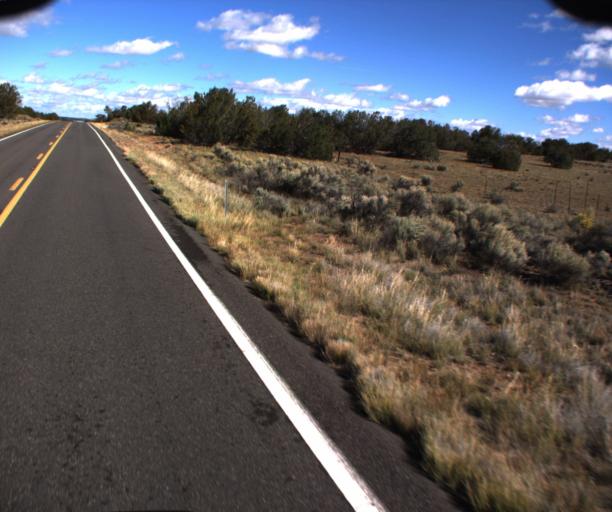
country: US
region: Arizona
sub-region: Apache County
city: Saint Johns
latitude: 34.8812
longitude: -109.2379
